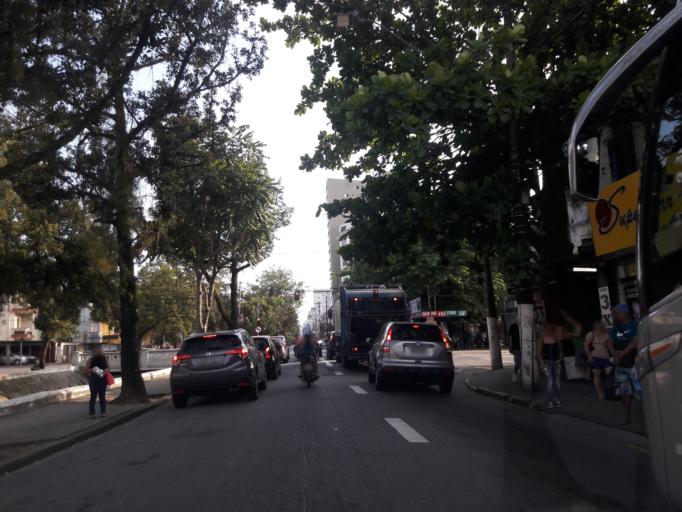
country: BR
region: Sao Paulo
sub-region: Santos
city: Santos
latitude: -23.9531
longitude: -46.3374
